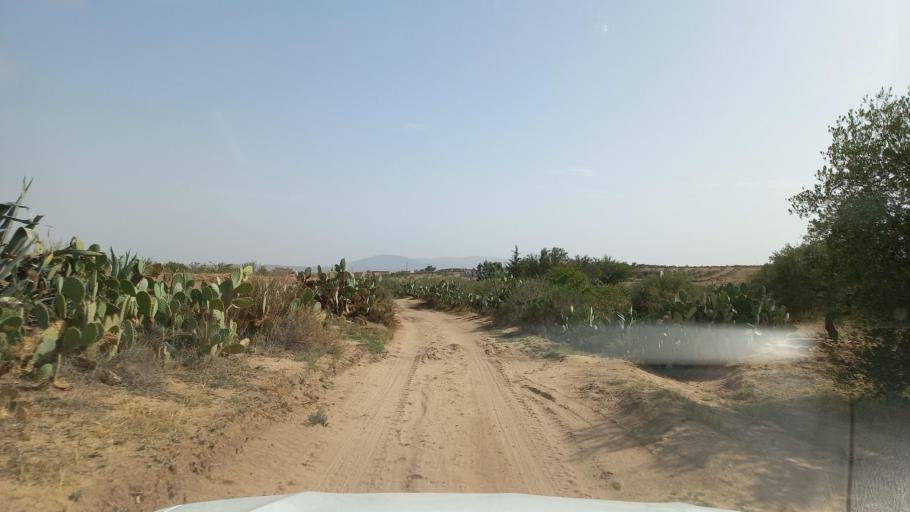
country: TN
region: Al Qasrayn
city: Kasserine
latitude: 35.3012
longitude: 8.9558
